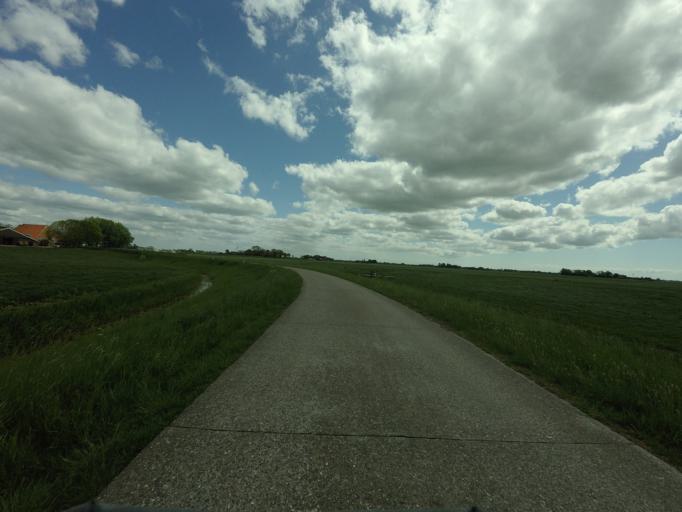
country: NL
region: Friesland
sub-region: Gemeente Littenseradiel
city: Wommels
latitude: 53.1142
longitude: 5.5506
